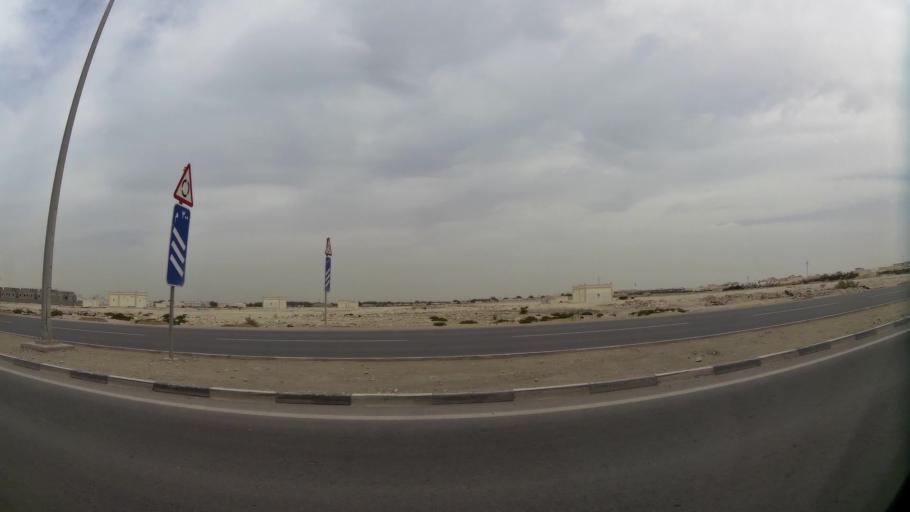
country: QA
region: Baladiyat ad Dawhah
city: Doha
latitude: 25.2334
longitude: 51.4707
